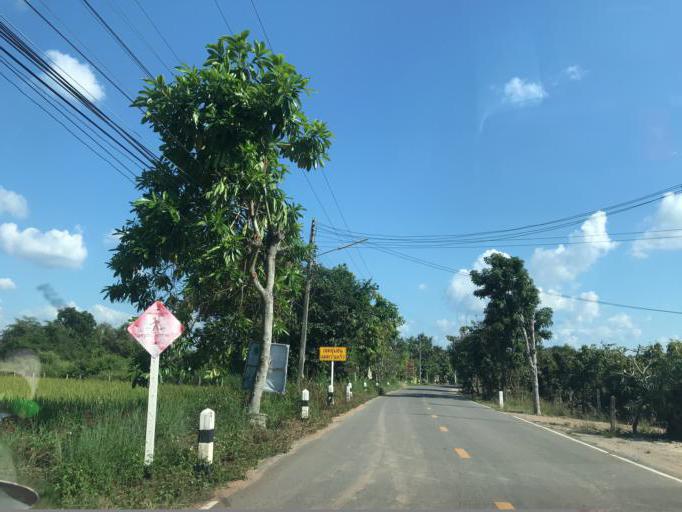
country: TH
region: Chiang Mai
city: Mae Wang
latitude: 18.5584
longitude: 98.8287
